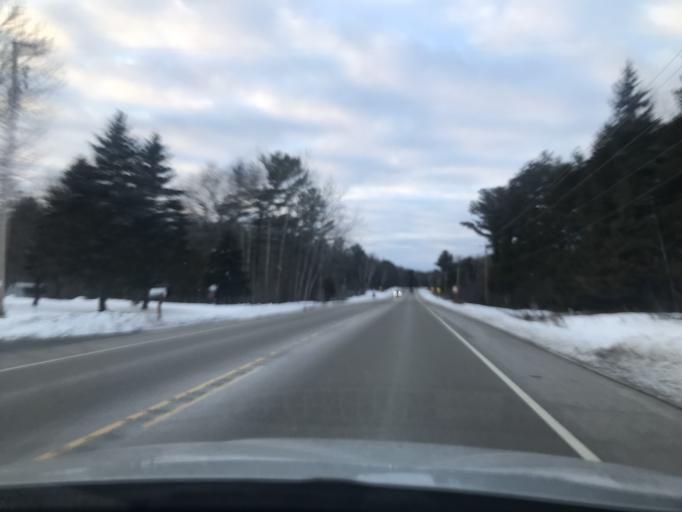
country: US
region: Wisconsin
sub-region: Marinette County
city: Marinette
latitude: 45.1135
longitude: -87.6750
